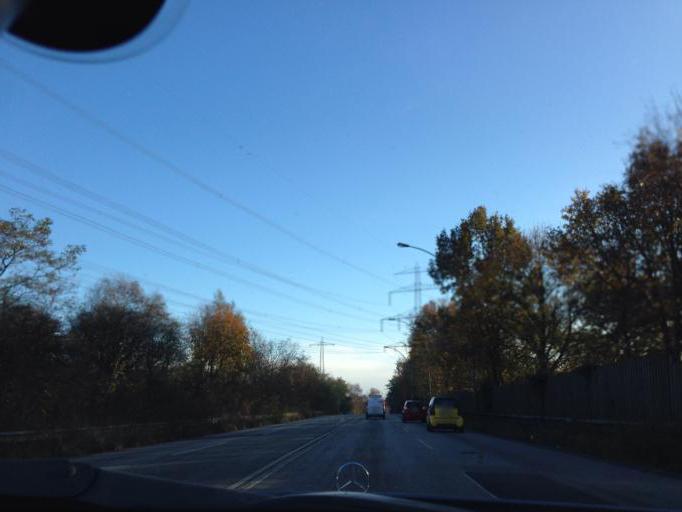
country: DE
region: Schleswig-Holstein
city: Stapelfeld
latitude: 53.6094
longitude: 10.1799
